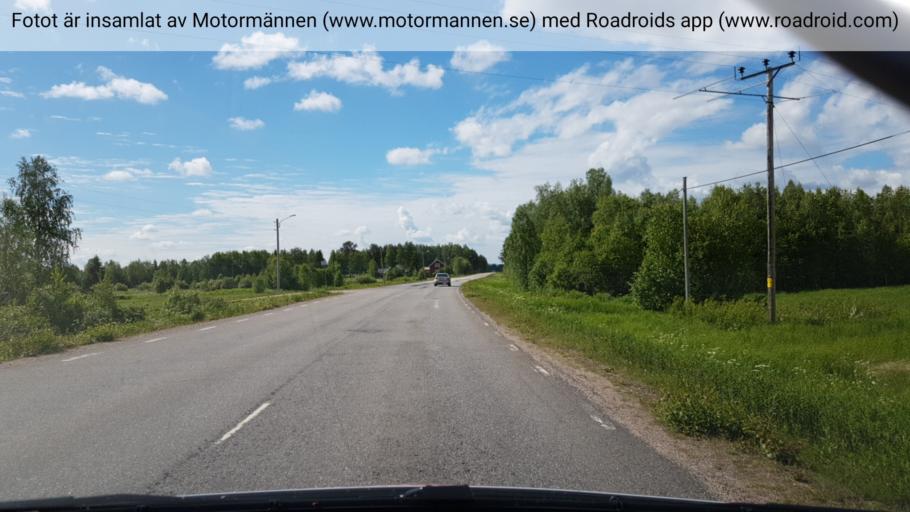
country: FI
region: Lapland
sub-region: Torniolaakso
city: Pello
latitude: 66.7842
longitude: 23.8932
